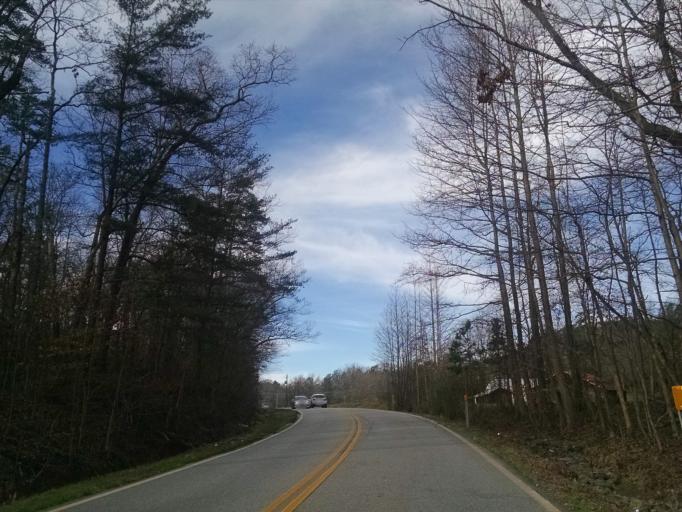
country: US
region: Georgia
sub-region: Gwinnett County
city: Sugar Hill
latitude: 34.0797
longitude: -84.0339
